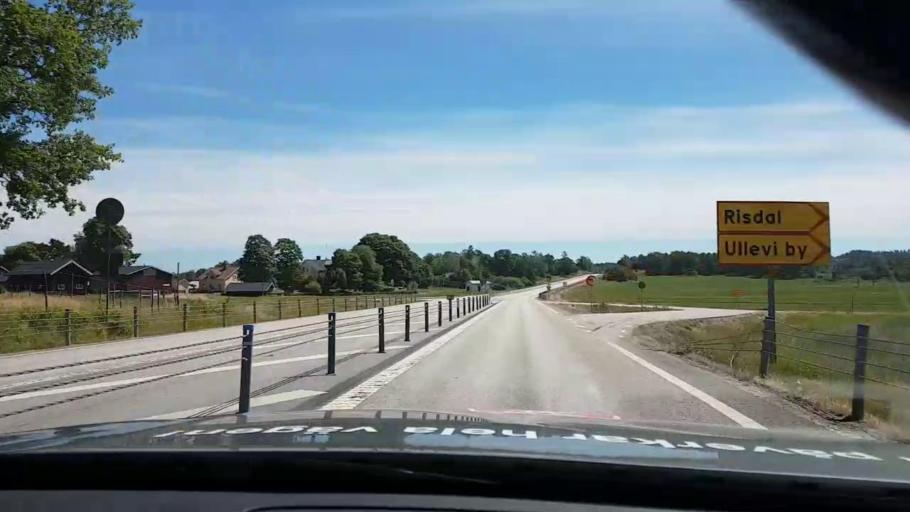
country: SE
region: Kalmar
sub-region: Vasterviks Kommun
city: Gamleby
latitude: 57.8799
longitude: 16.3959
